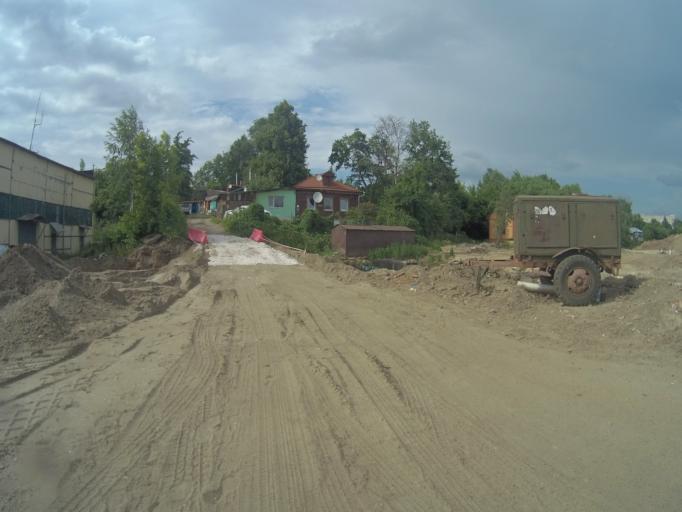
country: RU
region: Vladimir
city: Vladimir
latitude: 56.1329
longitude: 40.3977
